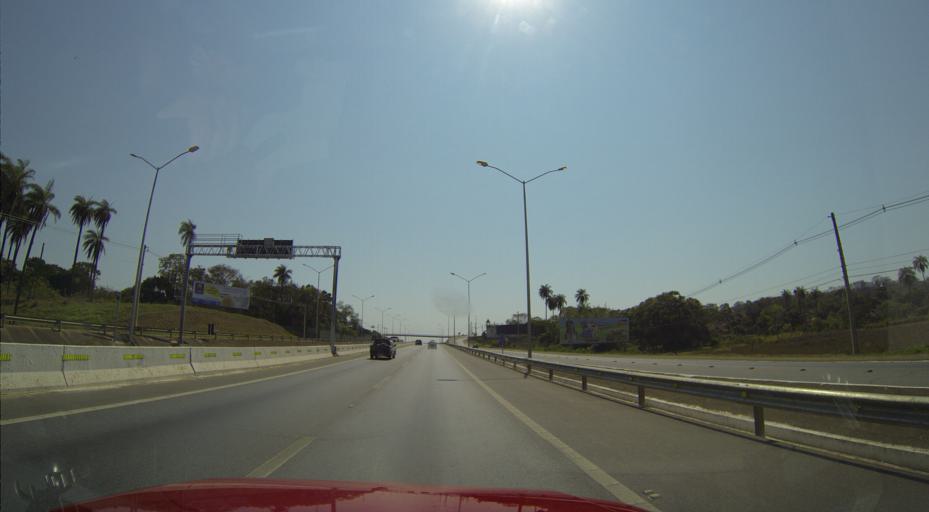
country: BR
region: Minas Gerais
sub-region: Vespasiano
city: Vespasiano
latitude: -19.7259
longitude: -43.9368
